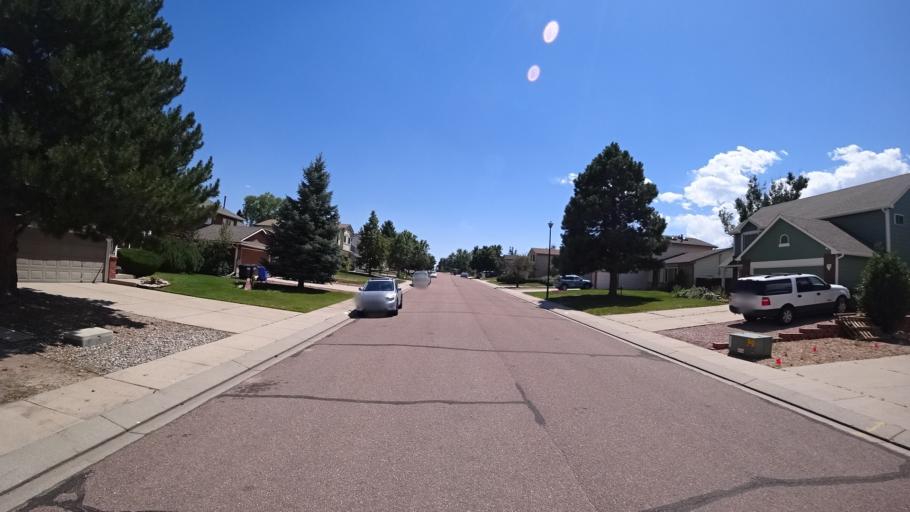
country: US
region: Colorado
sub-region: El Paso County
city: Black Forest
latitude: 38.9507
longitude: -104.7483
